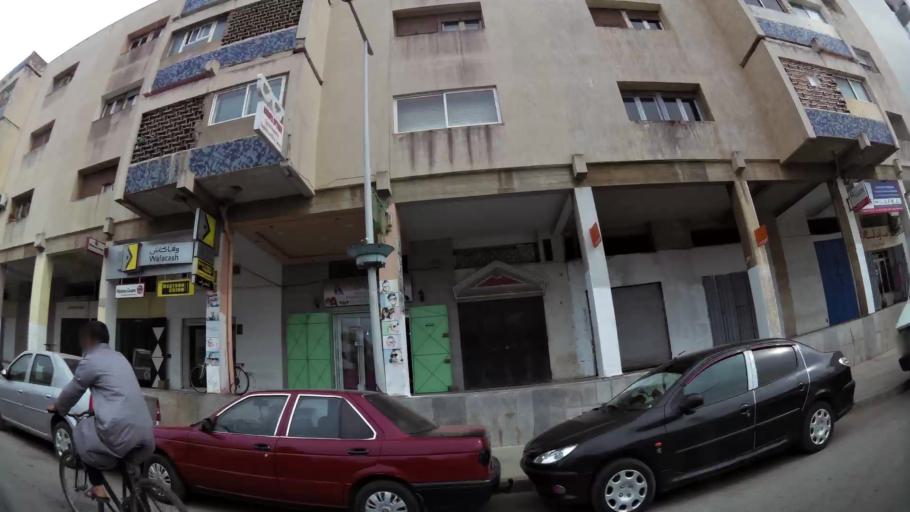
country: MA
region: Rabat-Sale-Zemmour-Zaer
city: Sale
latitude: 34.0459
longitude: -6.8055
